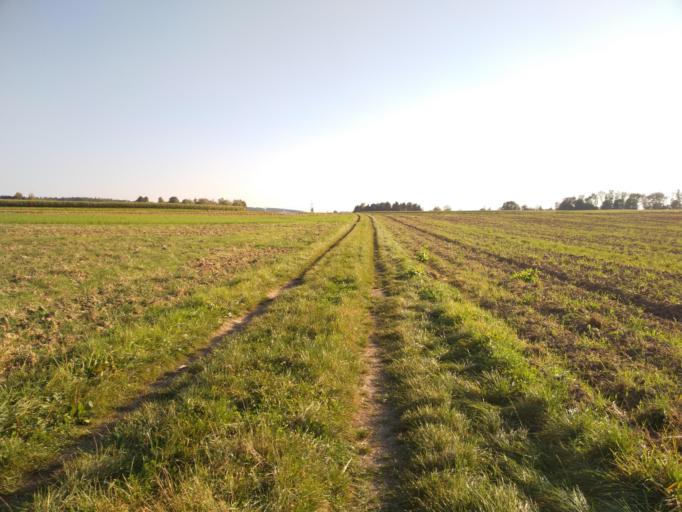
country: DE
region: Bavaria
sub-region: Swabia
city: Guenzburg
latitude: 48.4443
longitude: 10.2953
